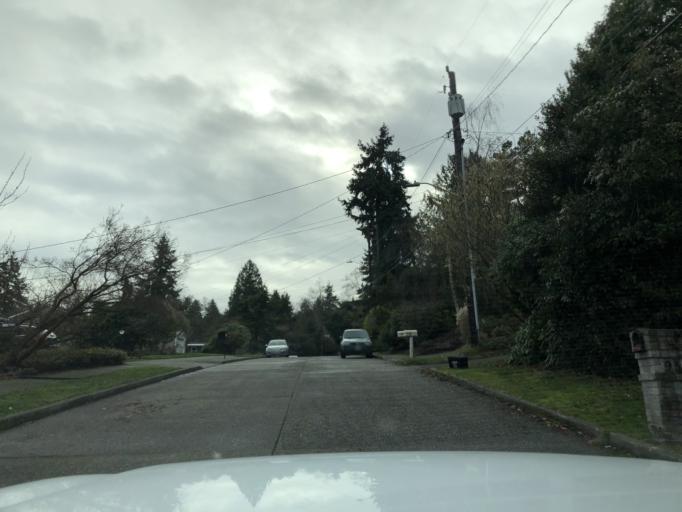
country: US
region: Washington
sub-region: King County
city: Inglewood-Finn Hill
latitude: 47.6984
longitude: -122.2814
